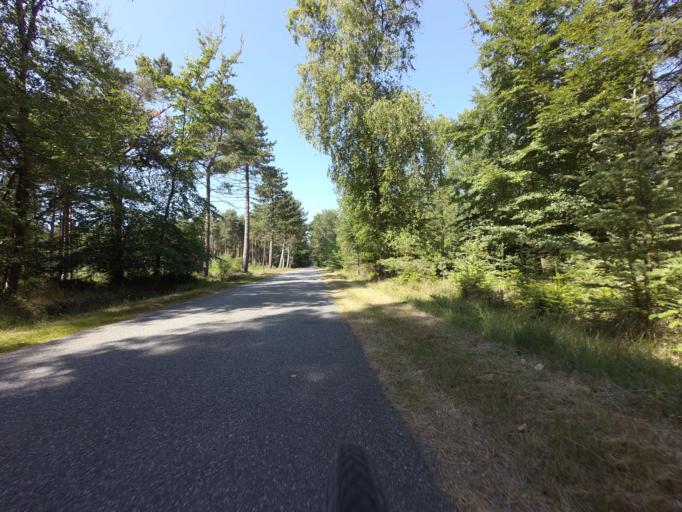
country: DK
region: North Denmark
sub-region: Laeso Kommune
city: Byrum
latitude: 57.2870
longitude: 11.0059
